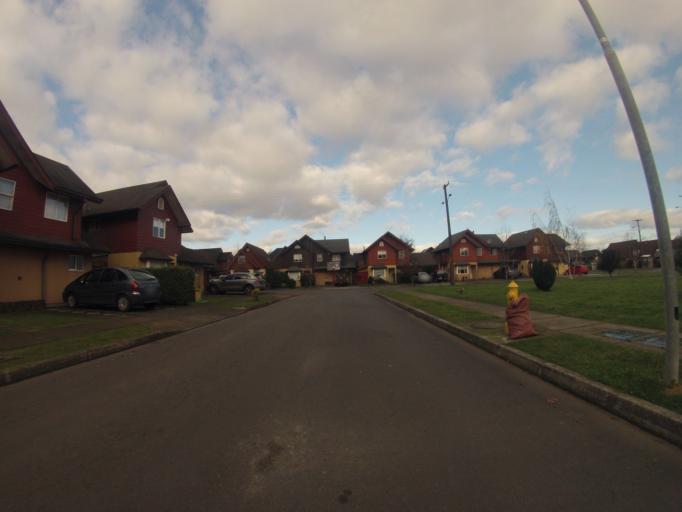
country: CL
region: Araucania
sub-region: Provincia de Cautin
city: Temuco
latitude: -38.7404
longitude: -72.6452
